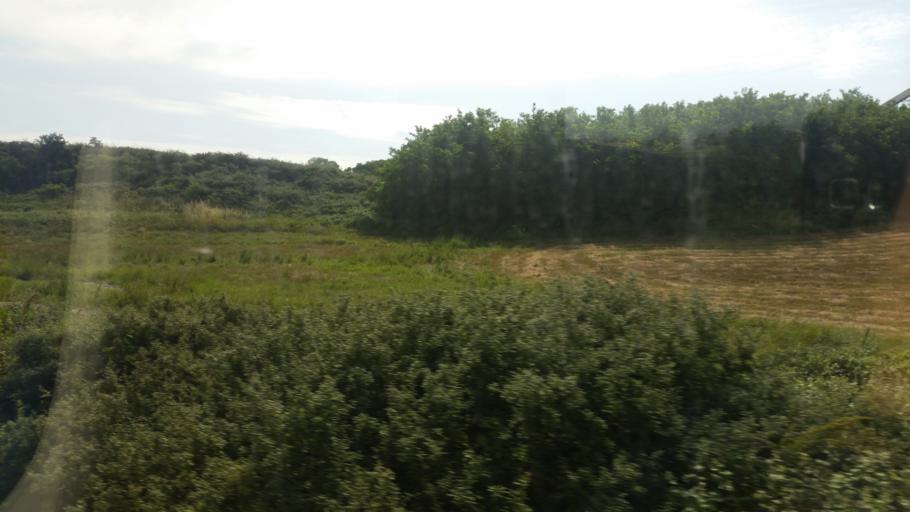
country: TR
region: Tekirdag
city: Velimese
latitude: 41.2145
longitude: 27.8423
